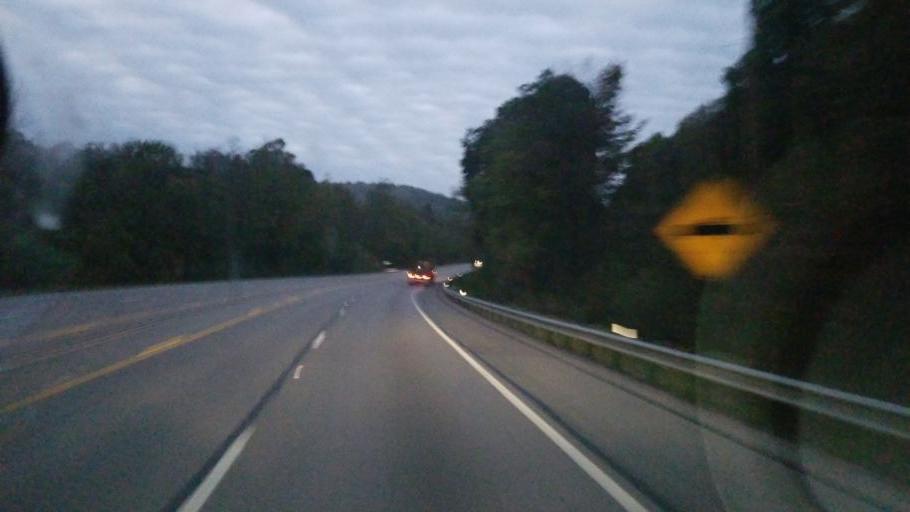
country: US
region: Ohio
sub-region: Pike County
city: Waverly
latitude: 39.2002
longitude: -82.9795
